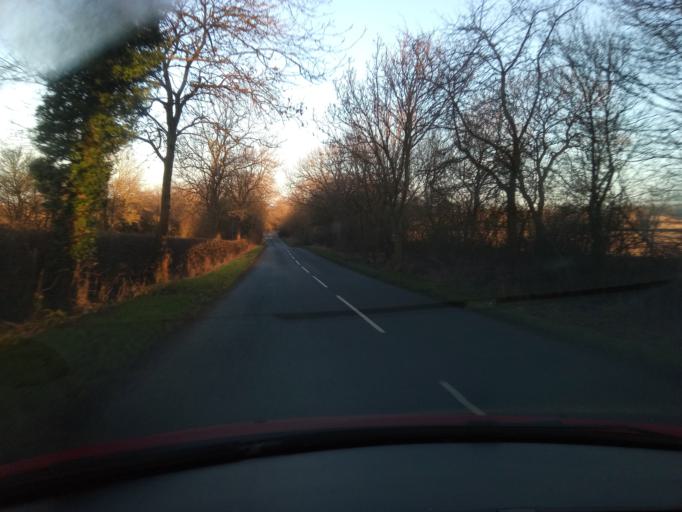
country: GB
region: England
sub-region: Leicestershire
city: Sileby
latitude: 52.7559
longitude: -1.0968
